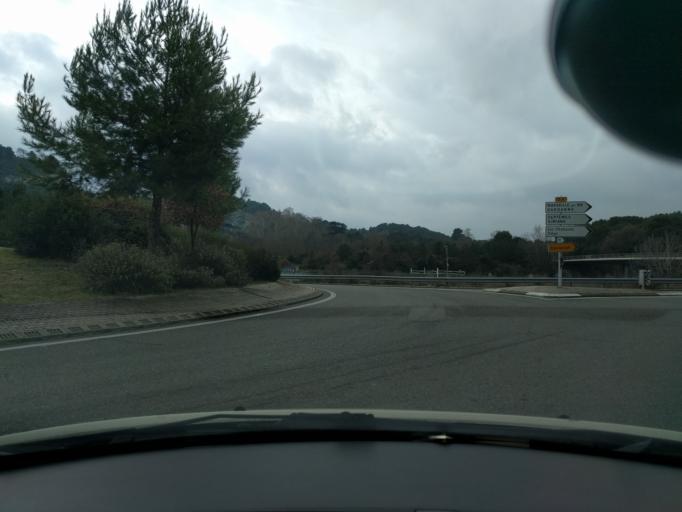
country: FR
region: Provence-Alpes-Cote d'Azur
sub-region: Departement des Bouches-du-Rhone
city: Bouc-Bel-Air
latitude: 43.4292
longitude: 5.4037
